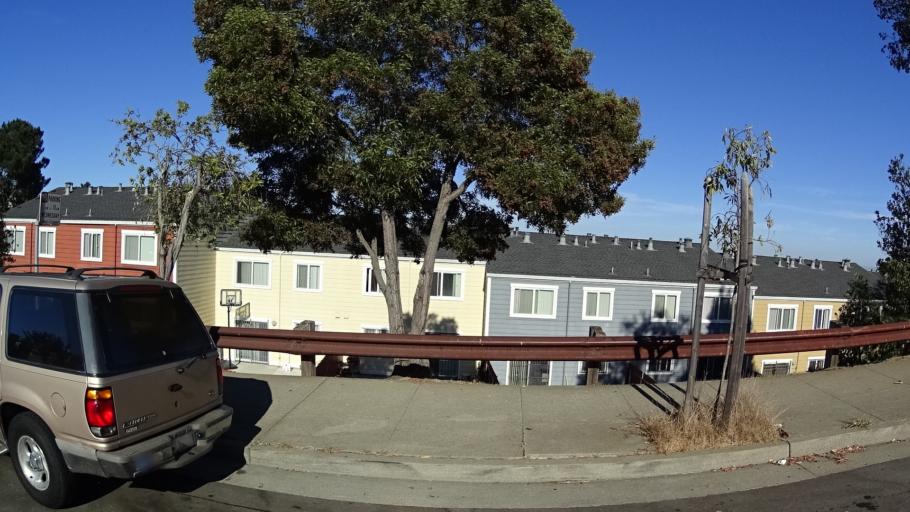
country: US
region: California
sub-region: San Francisco County
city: San Francisco
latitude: 37.7341
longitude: -122.3827
